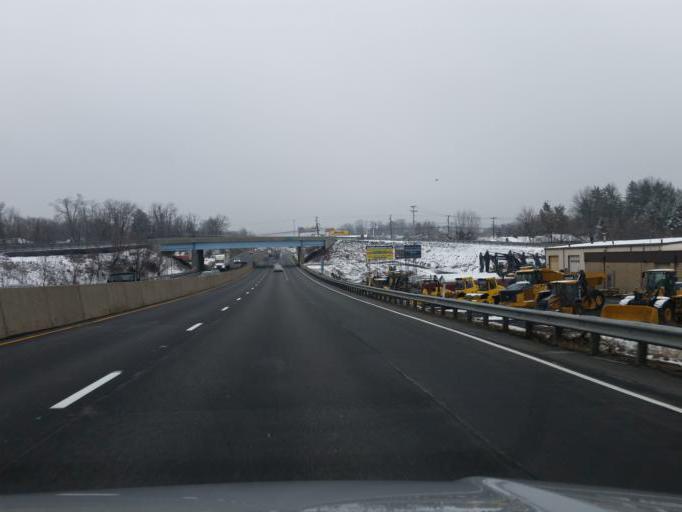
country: US
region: Pennsylvania
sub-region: York County
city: Valley Green
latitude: 40.1689
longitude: -76.8306
